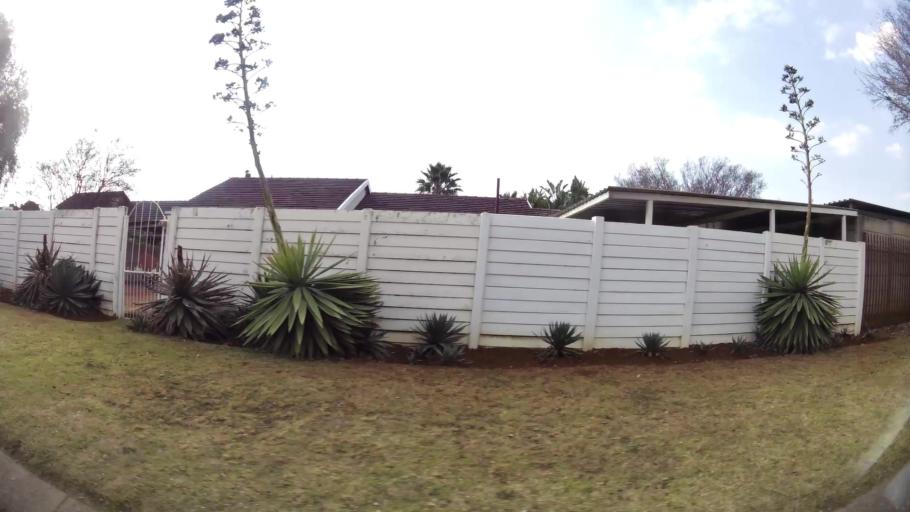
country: ZA
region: Gauteng
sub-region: City of Johannesburg Metropolitan Municipality
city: Modderfontein
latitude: -26.1126
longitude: 28.2058
